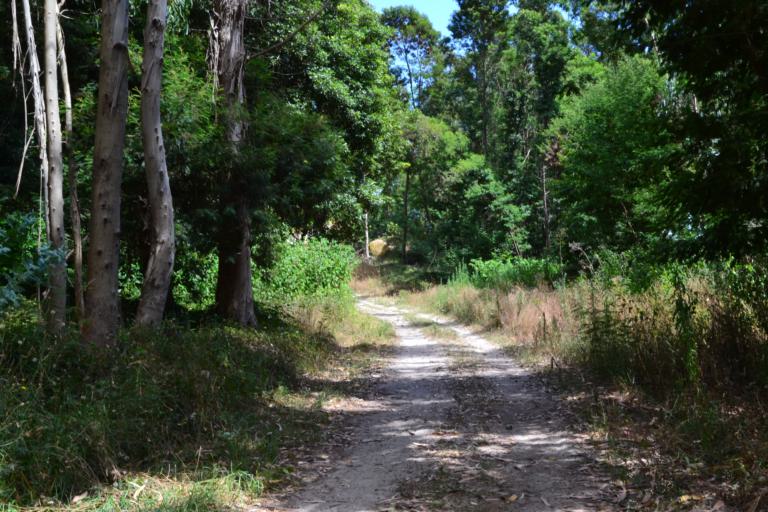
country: PT
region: Viana do Castelo
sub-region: Viana do Castelo
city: Viana do Castelo
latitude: 41.7031
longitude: -8.8374
